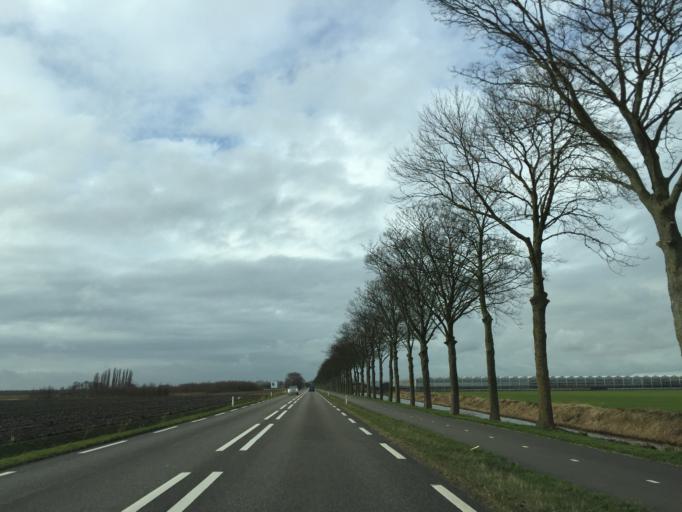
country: NL
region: South Holland
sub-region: Gemeente Boskoop
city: Boskoop
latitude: 52.0766
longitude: 4.6227
